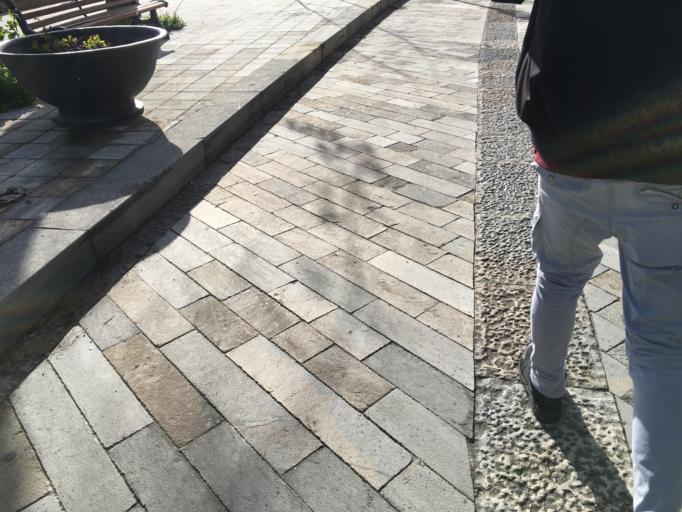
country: IT
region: Sicily
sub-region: Palermo
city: Polizzi Generosa
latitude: 37.8126
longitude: 14.0035
